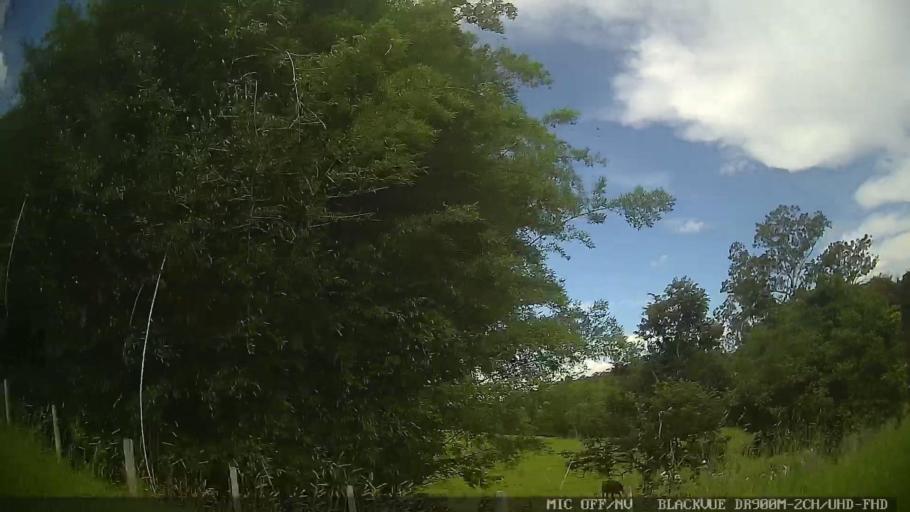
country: BR
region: Sao Paulo
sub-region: Conchas
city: Conchas
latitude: -23.0004
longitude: -47.9996
